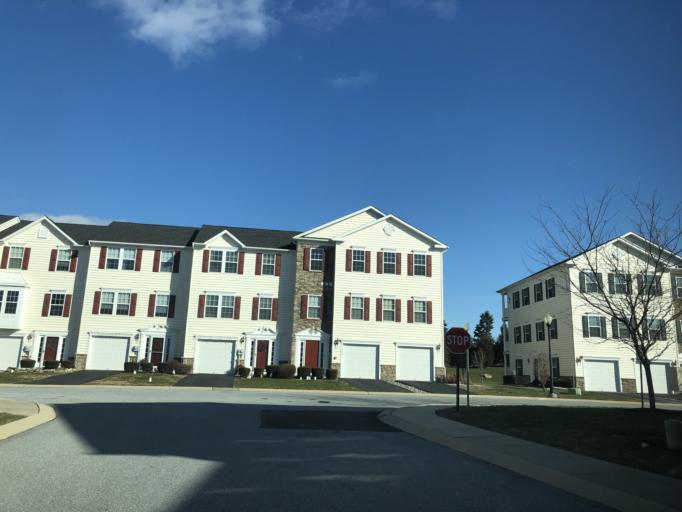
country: US
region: Pennsylvania
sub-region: Chester County
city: Parkesburg
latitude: 39.9856
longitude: -75.8764
